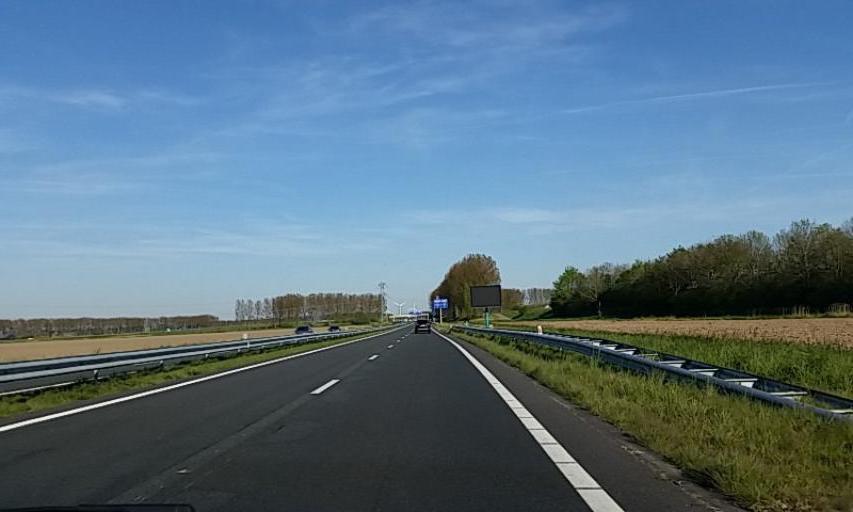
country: NL
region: Zeeland
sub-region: Gemeente Terneuzen
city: Sluiskil
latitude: 51.2975
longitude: 3.7950
